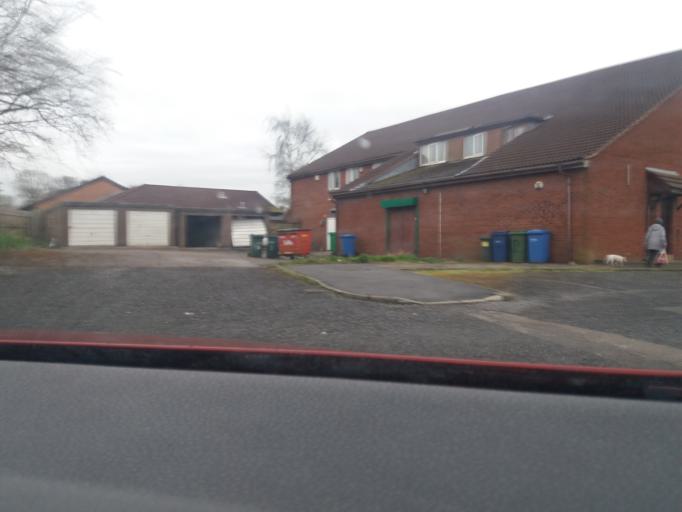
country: GB
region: England
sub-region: Lancashire
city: Chorley
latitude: 53.6392
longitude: -2.6382
